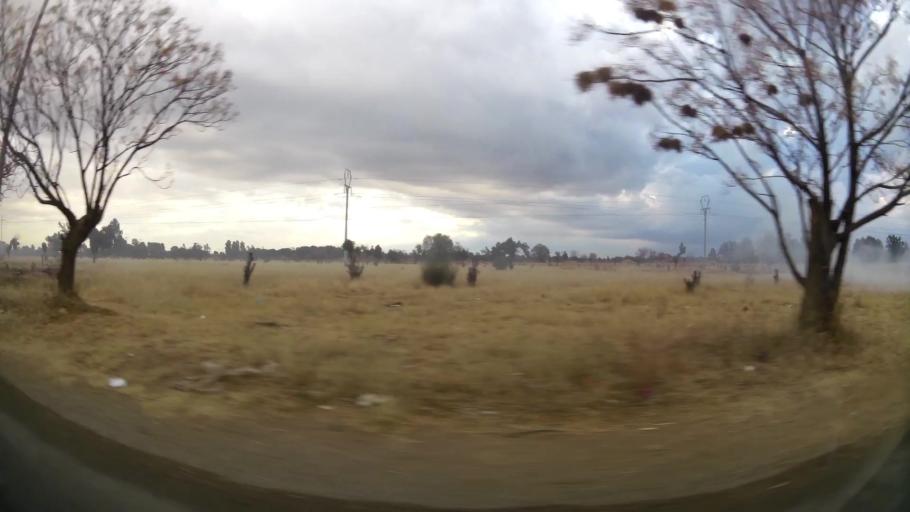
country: ZA
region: Orange Free State
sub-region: Lejweleputswa District Municipality
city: Welkom
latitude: -27.9575
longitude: 26.7196
